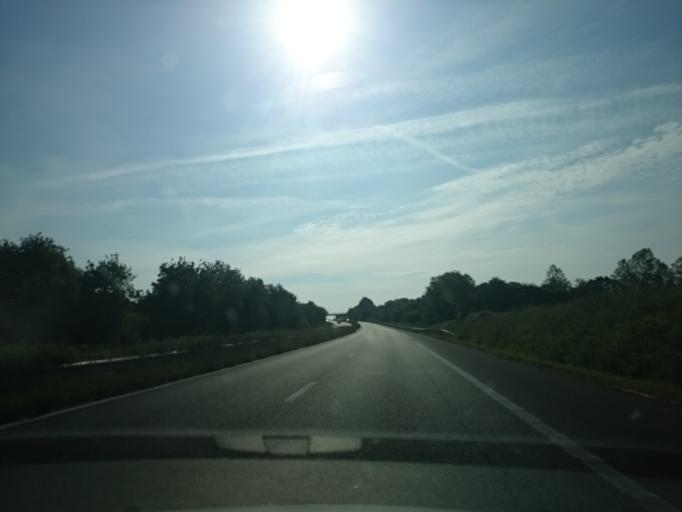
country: FR
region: Brittany
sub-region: Departement du Finistere
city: Le Trevoux
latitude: 47.8773
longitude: -3.6575
